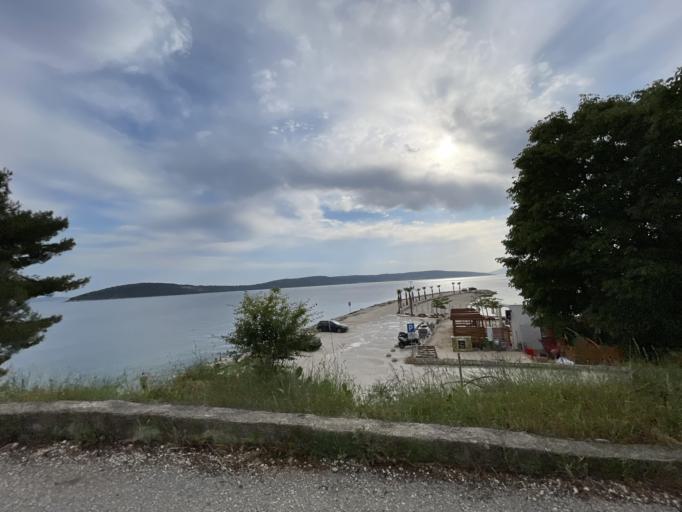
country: HR
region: Splitsko-Dalmatinska
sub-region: Grad Split
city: Split
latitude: 43.5052
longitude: 16.4013
